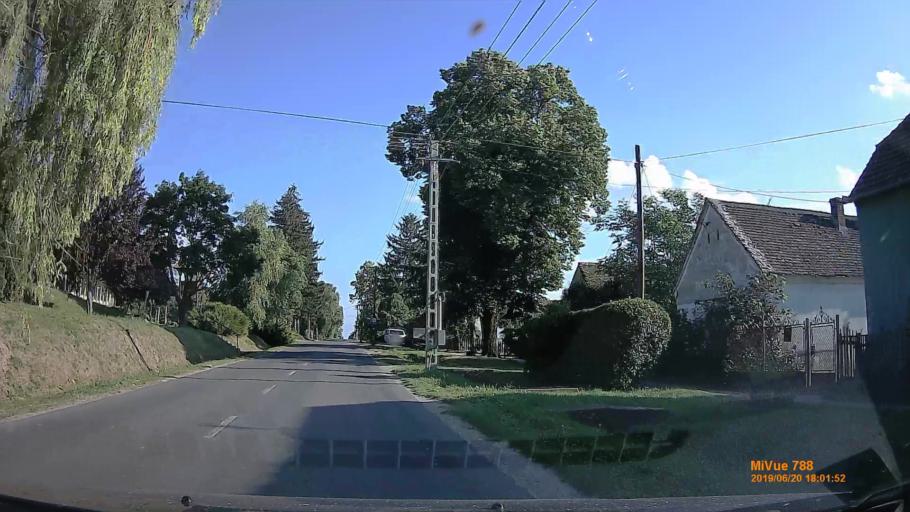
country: HU
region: Baranya
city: Buekkoesd
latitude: 46.0795
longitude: 17.9906
